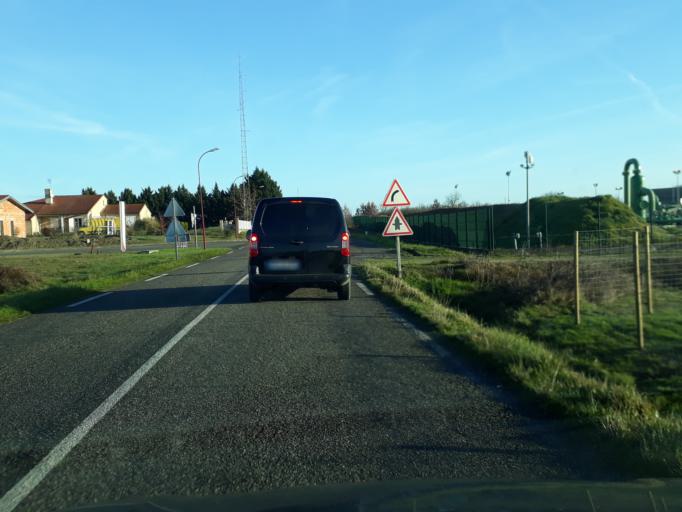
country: FR
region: Midi-Pyrenees
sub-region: Departement du Gers
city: Pujaudran
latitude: 43.5791
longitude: 1.1316
